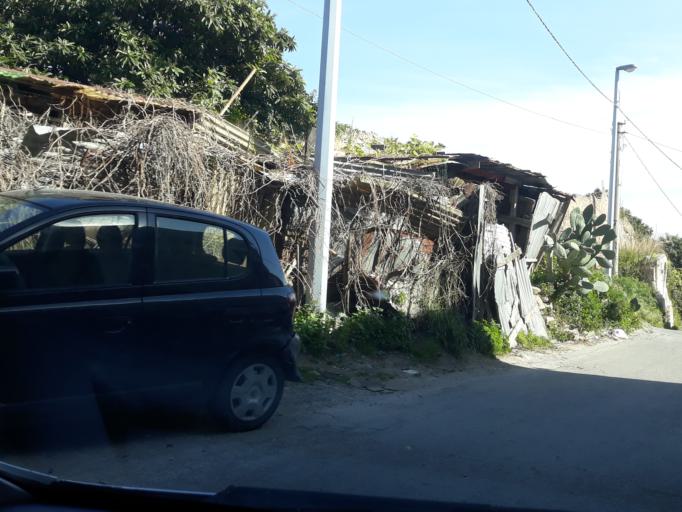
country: IT
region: Sicily
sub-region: Palermo
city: Palermo
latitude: 38.1060
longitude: 13.3282
